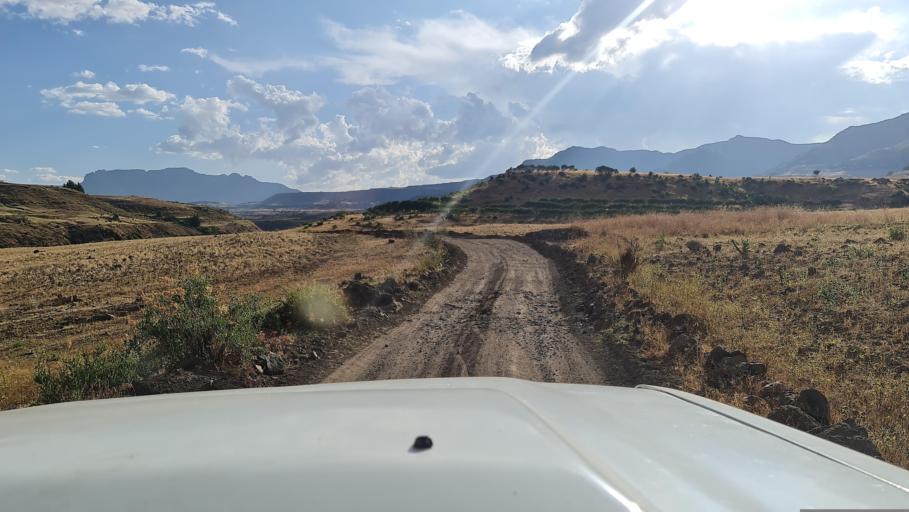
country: ET
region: Amhara
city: Debark'
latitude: 13.0834
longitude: 38.0116
